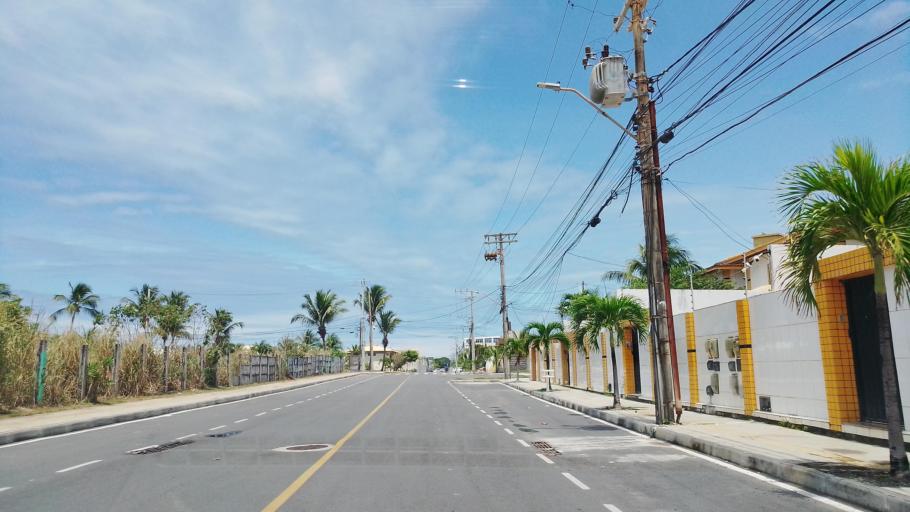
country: BR
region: Bahia
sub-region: Lauro De Freitas
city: Lauro de Freitas
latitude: -12.9351
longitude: -38.3289
